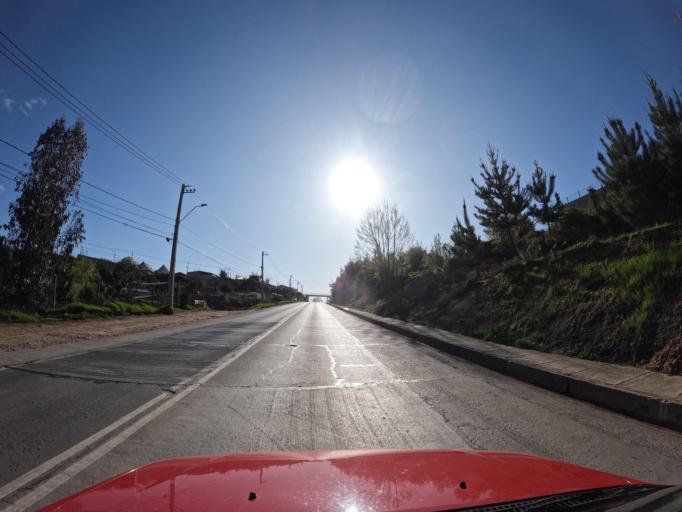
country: CL
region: Maule
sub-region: Provincia de Talca
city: Constitucion
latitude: -35.4519
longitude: -72.2767
